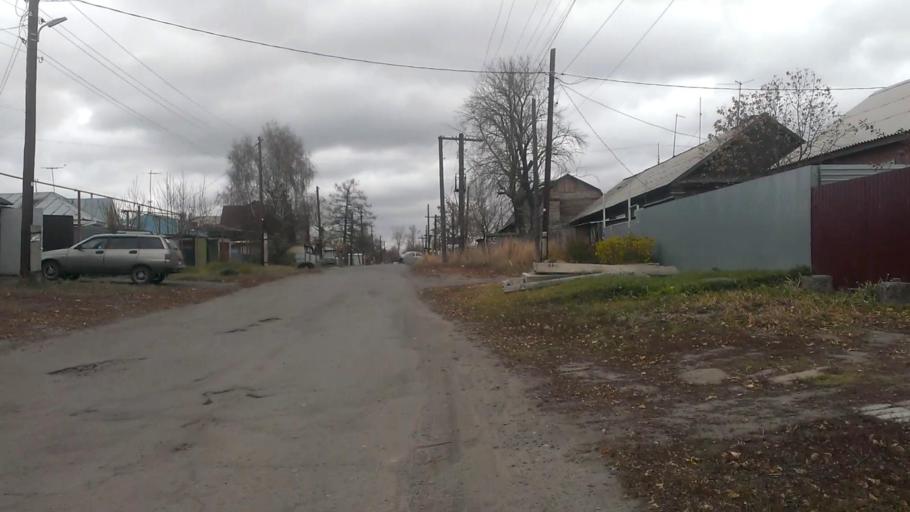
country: RU
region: Altai Krai
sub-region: Gorod Barnaulskiy
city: Barnaul
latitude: 53.3514
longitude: 83.7522
